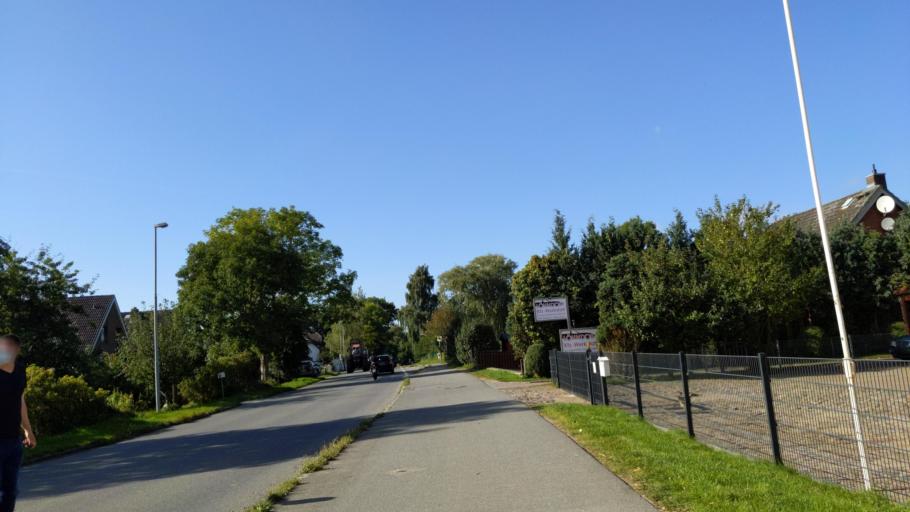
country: DE
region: Schleswig-Holstein
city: Stockelsdorf
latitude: 53.9498
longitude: 10.6249
